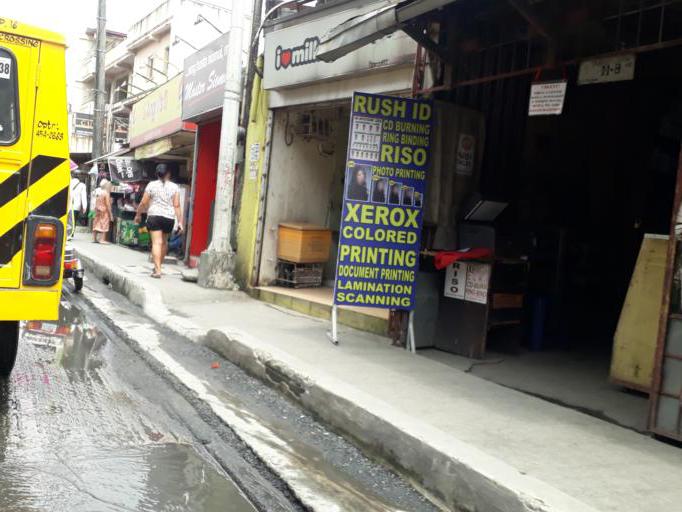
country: PH
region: Calabarzon
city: Bagong Pagasa
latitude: 14.6799
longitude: 121.0202
